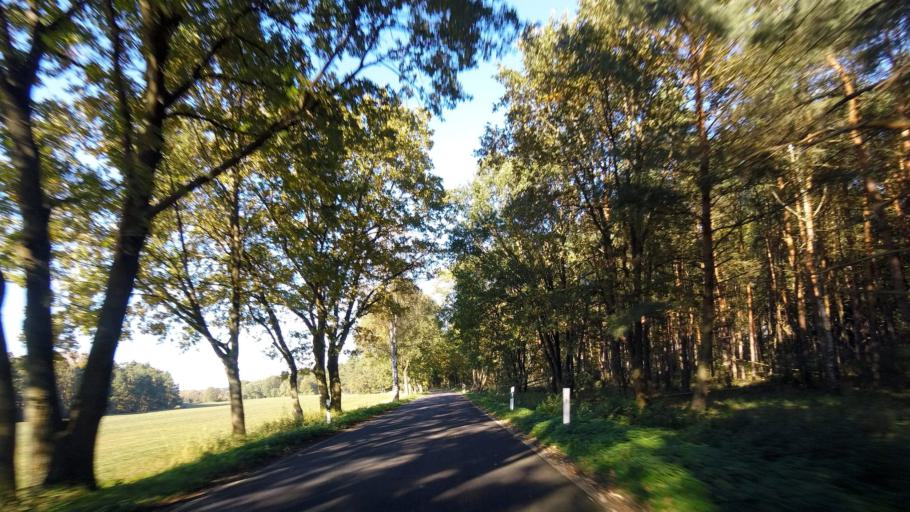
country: DE
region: Saxony-Anhalt
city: Kropstadt
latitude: 51.9654
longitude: 12.7879
